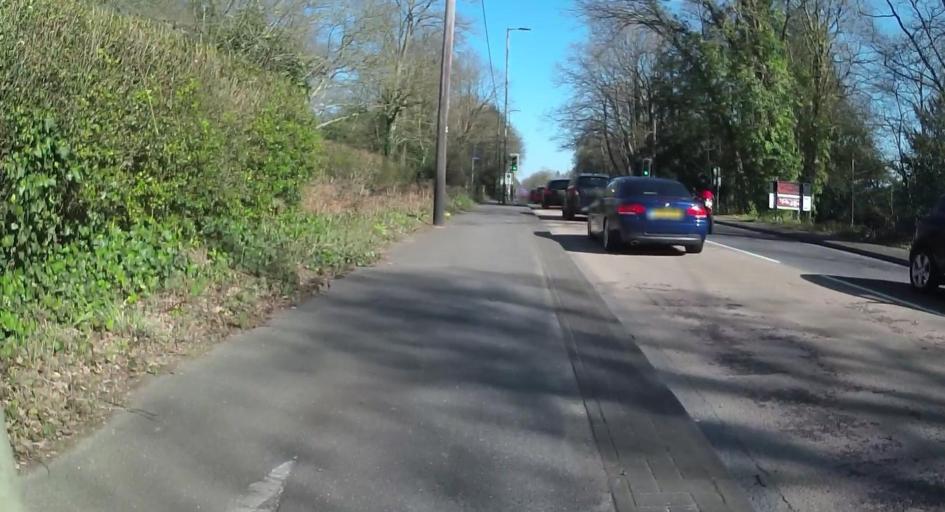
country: GB
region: England
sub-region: Bracknell Forest
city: Bracknell
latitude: 51.4128
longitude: -0.7231
